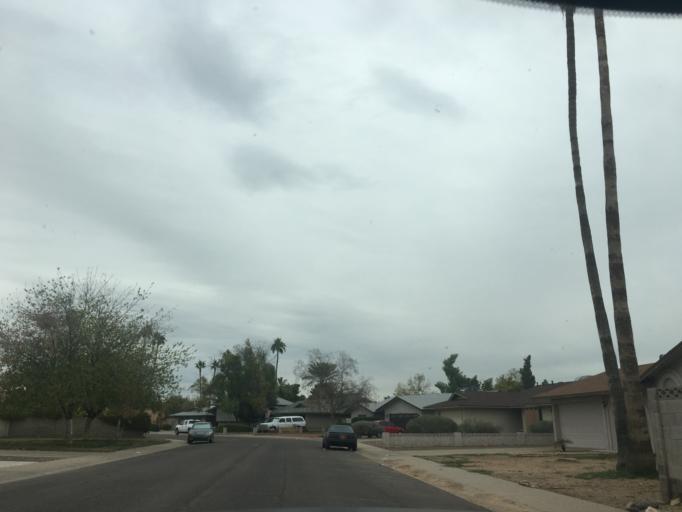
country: US
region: Arizona
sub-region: Maricopa County
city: Tempe
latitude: 33.3824
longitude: -111.9220
